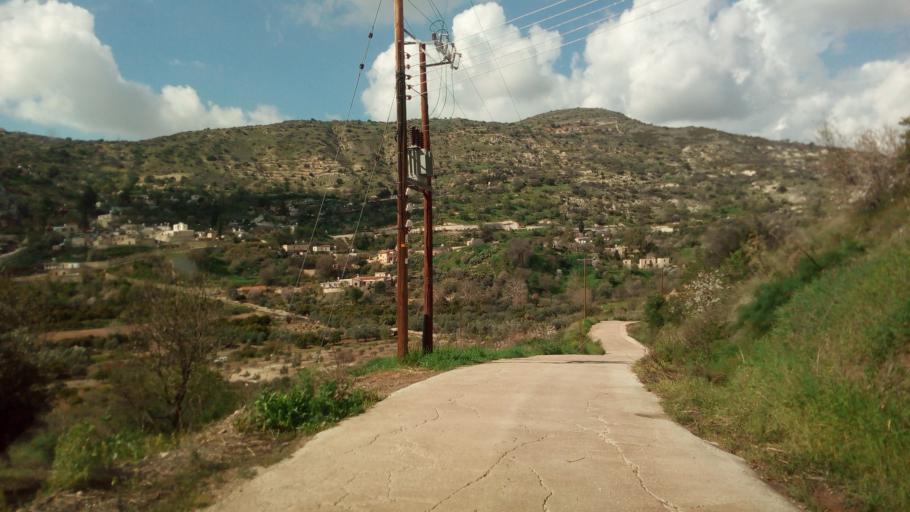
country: CY
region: Pafos
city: Mesogi
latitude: 34.7959
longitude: 32.5317
